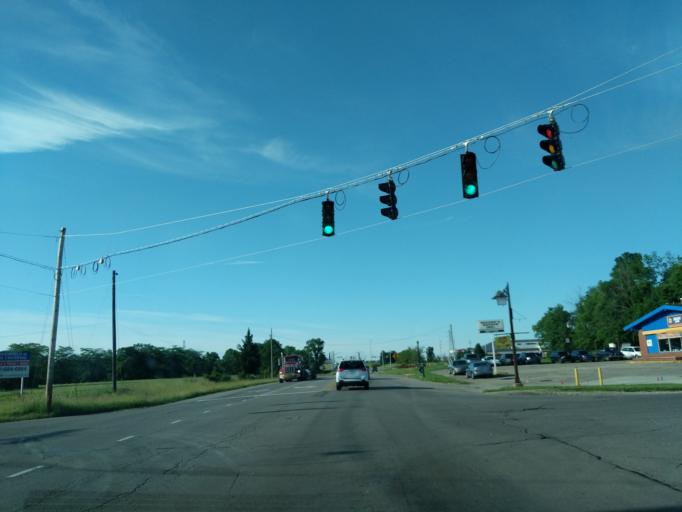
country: US
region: Indiana
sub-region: Hancock County
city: Greenfield
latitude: 39.8288
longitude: -85.7702
